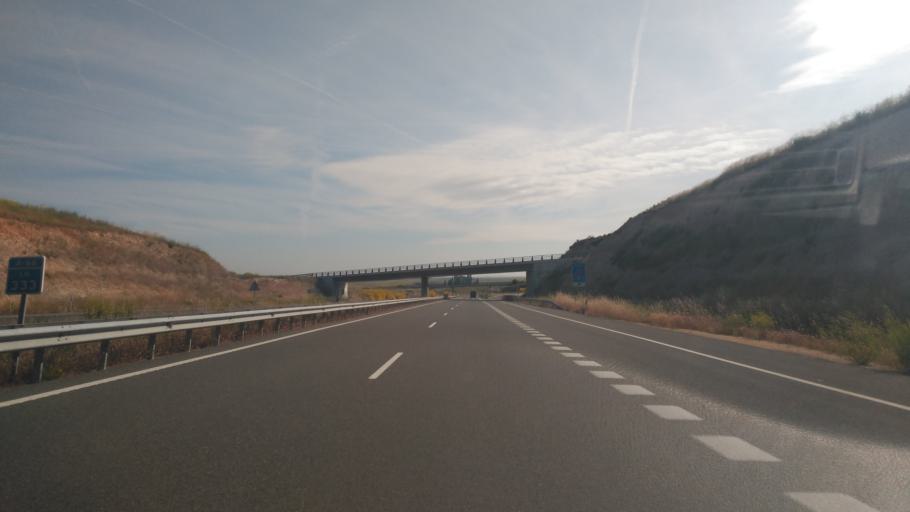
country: ES
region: Castille and Leon
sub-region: Provincia de Salamanca
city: Castellanos de Villiquera
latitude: 41.0296
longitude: -5.6747
